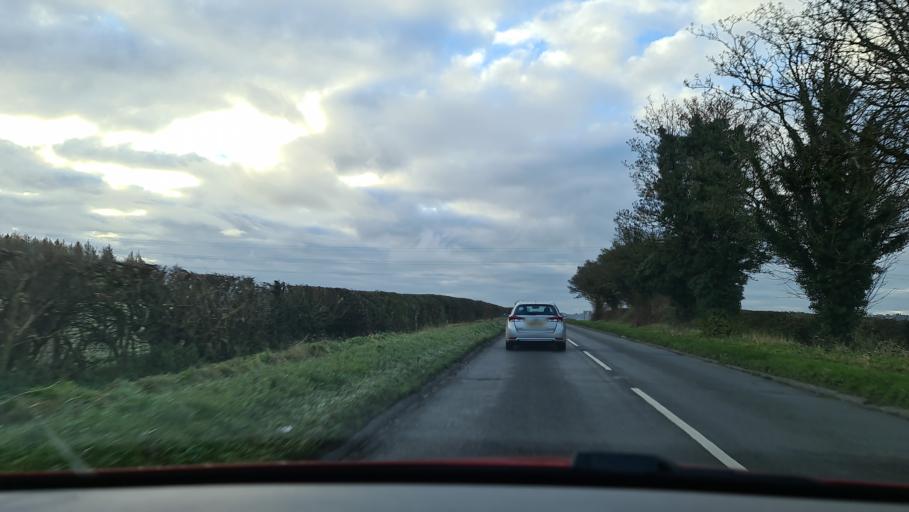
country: GB
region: England
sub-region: Buckinghamshire
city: Princes Risborough
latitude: 51.7076
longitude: -0.8335
